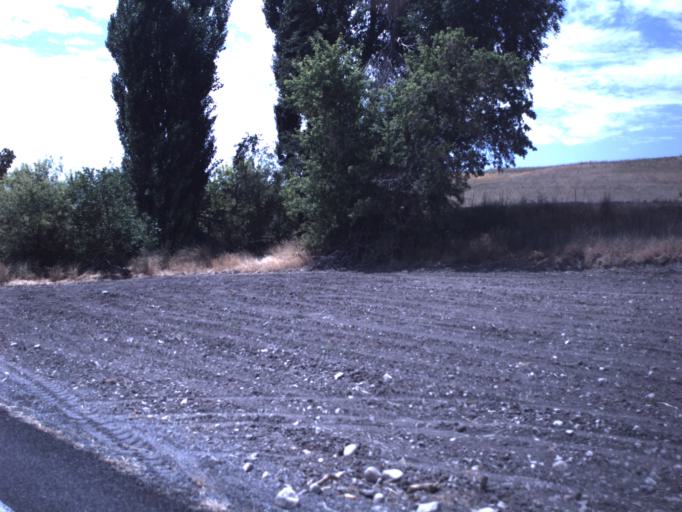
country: US
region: Utah
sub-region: Box Elder County
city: Tremonton
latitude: 41.6669
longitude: -112.2965
